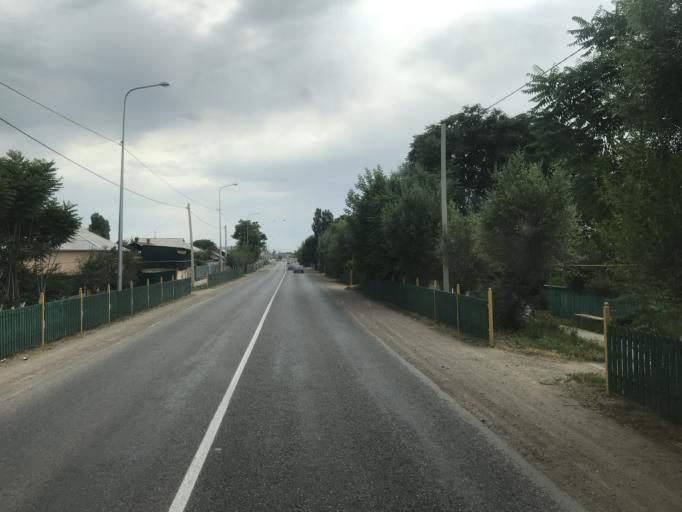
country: KZ
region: Ongtustik Qazaqstan
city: Saryaghash
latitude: 41.3499
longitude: 68.9639
